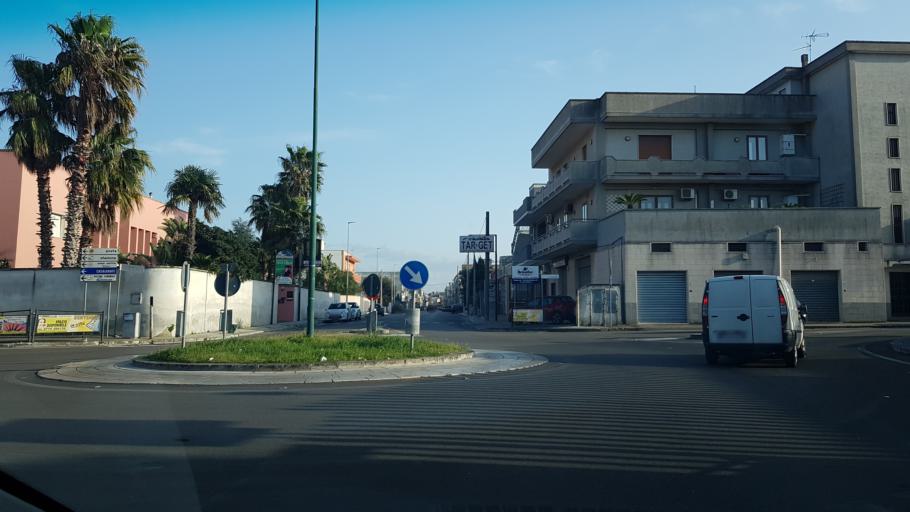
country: IT
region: Apulia
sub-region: Provincia di Lecce
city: Trepuzzi
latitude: 40.4100
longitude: 18.0669
